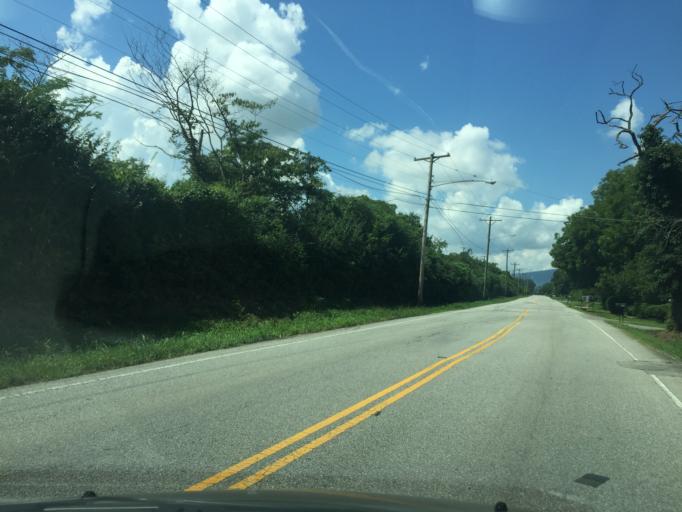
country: US
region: Tennessee
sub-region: Hamilton County
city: East Chattanooga
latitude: 35.0679
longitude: -85.2648
